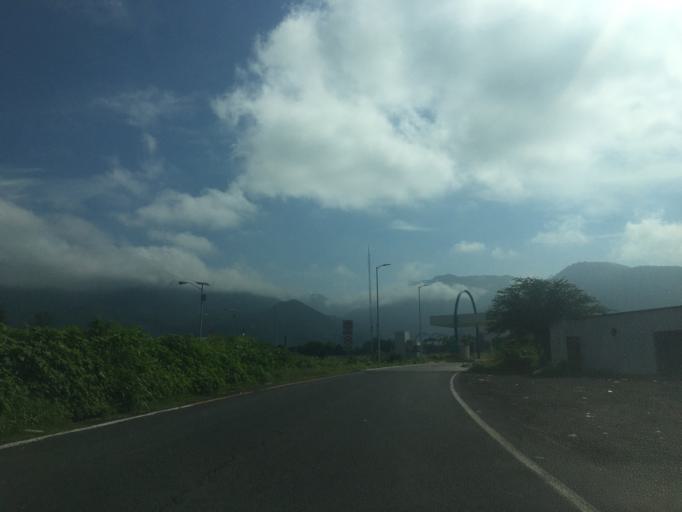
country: MX
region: Nayarit
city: Jala
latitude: 21.0884
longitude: -104.4401
